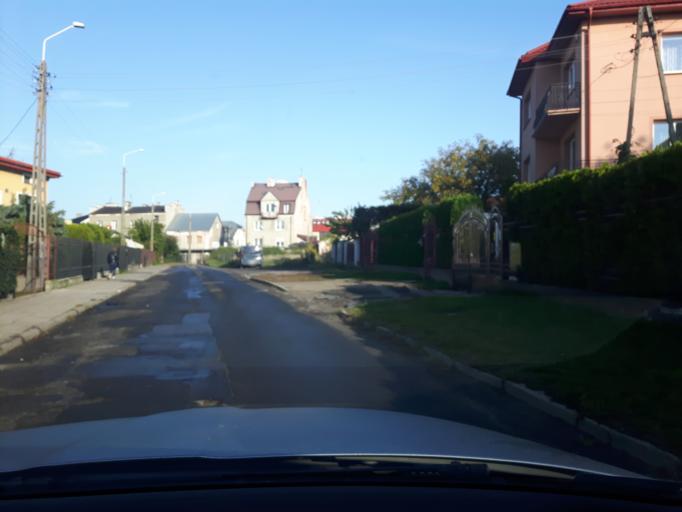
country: PL
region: Masovian Voivodeship
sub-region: Powiat wolominski
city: Zabki
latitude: 52.2877
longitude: 21.1127
